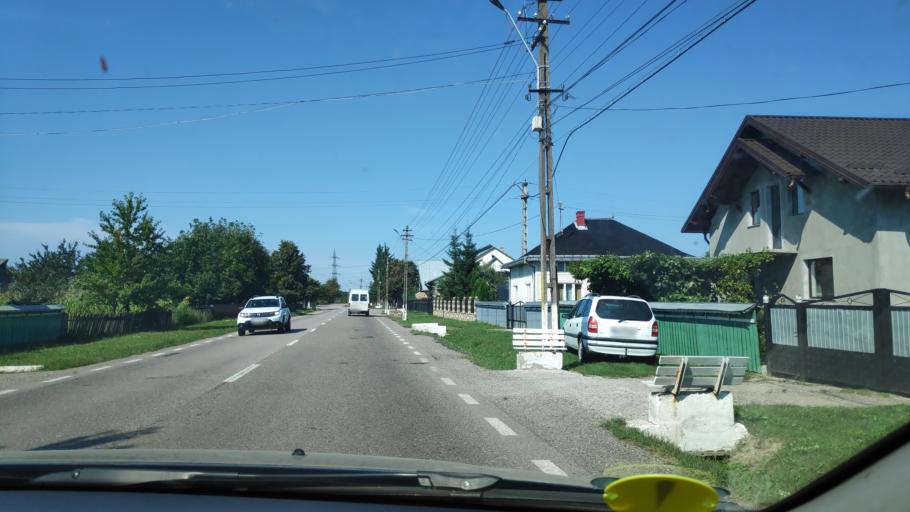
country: RO
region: Suceava
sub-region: Comuna Boroaia
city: Boroaia
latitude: 47.3541
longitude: 26.3413
